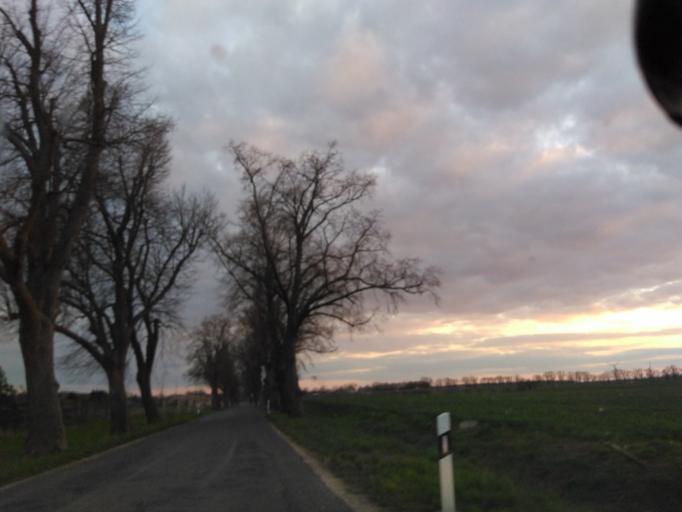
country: DE
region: Brandenburg
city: Protzel
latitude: 52.6575
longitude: 14.0696
